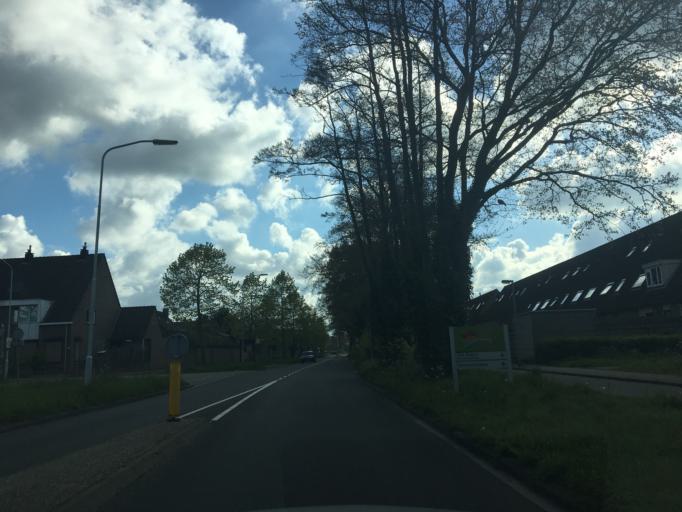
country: NL
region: Gelderland
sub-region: Gemeente Ede
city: Ede
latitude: 52.0181
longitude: 5.6581
